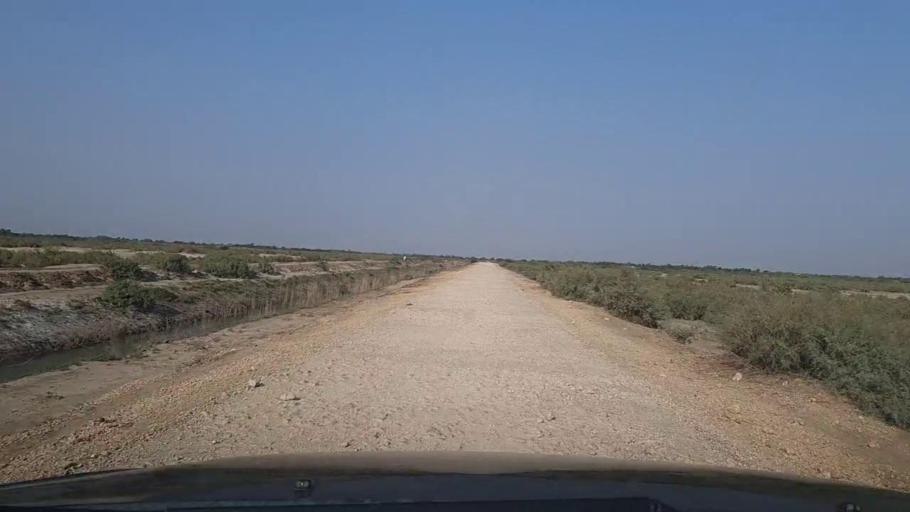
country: PK
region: Sindh
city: Mirpur Sakro
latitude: 24.6463
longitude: 67.7540
